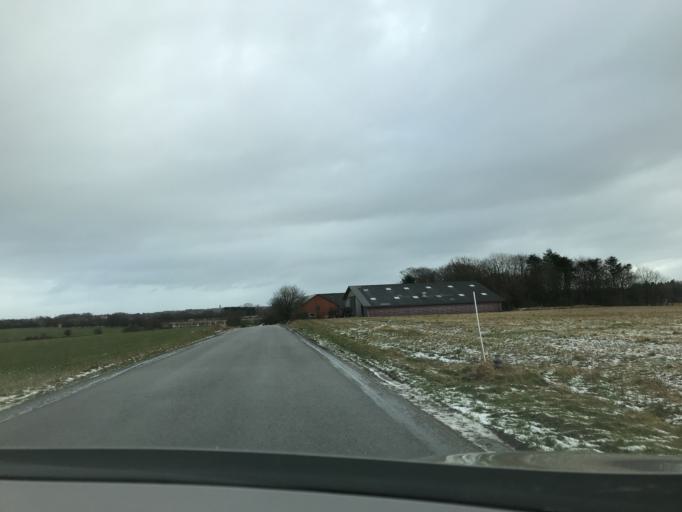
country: DK
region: South Denmark
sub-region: Varde Kommune
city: Varde
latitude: 55.6581
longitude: 8.4336
